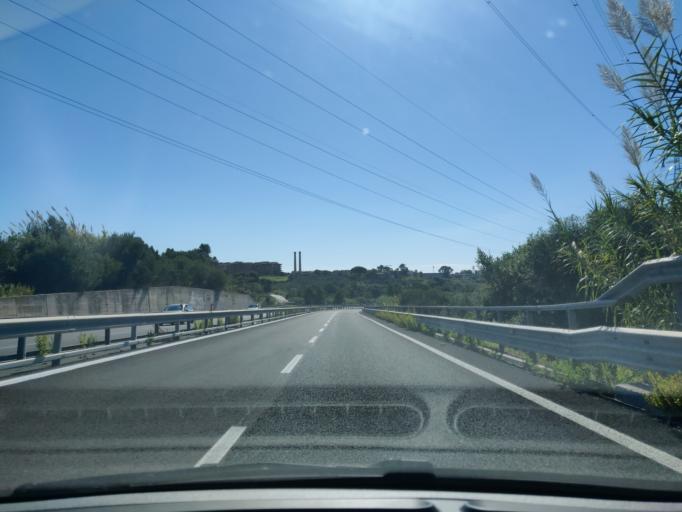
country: IT
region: Latium
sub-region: Citta metropolitana di Roma Capitale
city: Civitavecchia
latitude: 42.1101
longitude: 11.7924
